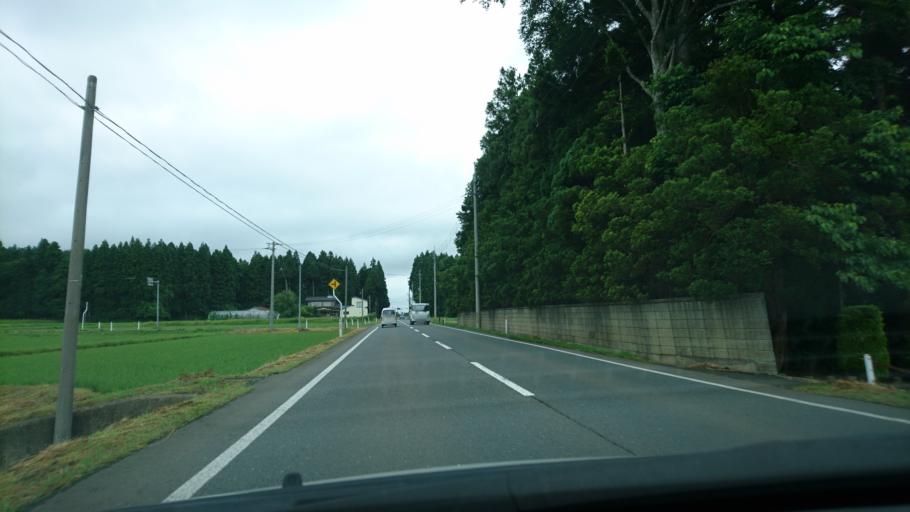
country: JP
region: Iwate
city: Mizusawa
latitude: 39.1158
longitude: 141.0529
